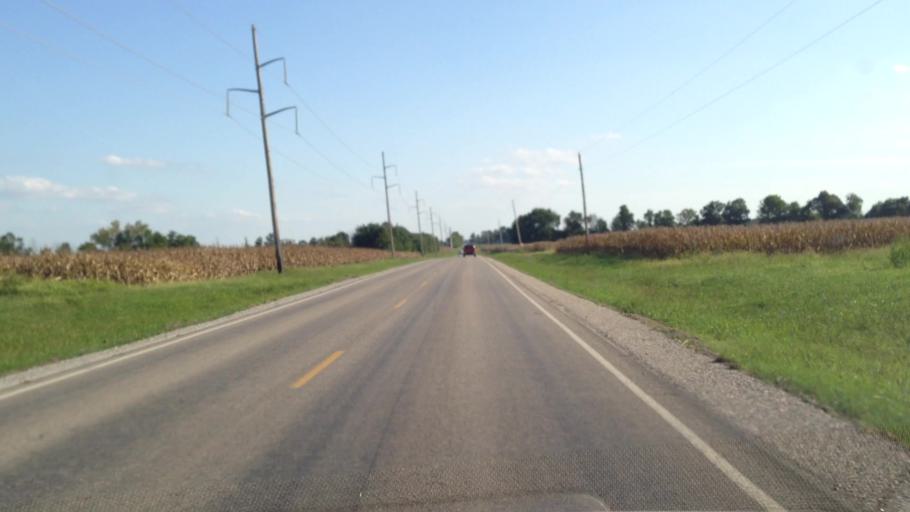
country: US
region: Kansas
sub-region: Crawford County
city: Pittsburg
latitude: 37.3749
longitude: -94.6314
